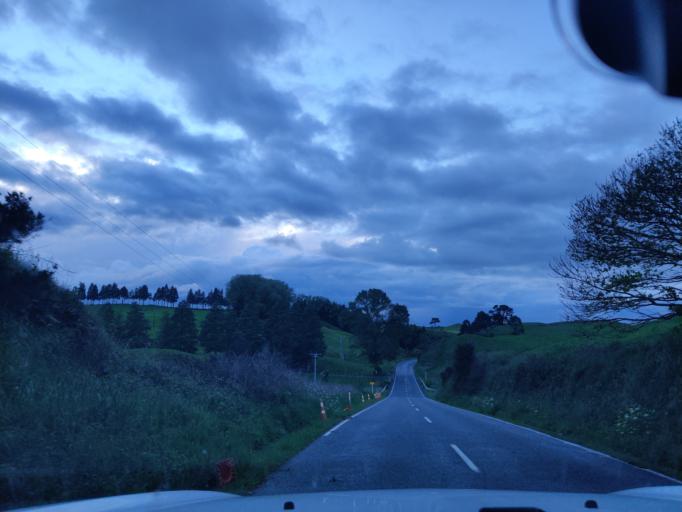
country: NZ
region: Waikato
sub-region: South Waikato District
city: Tokoroa
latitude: -38.1893
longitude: 175.7975
